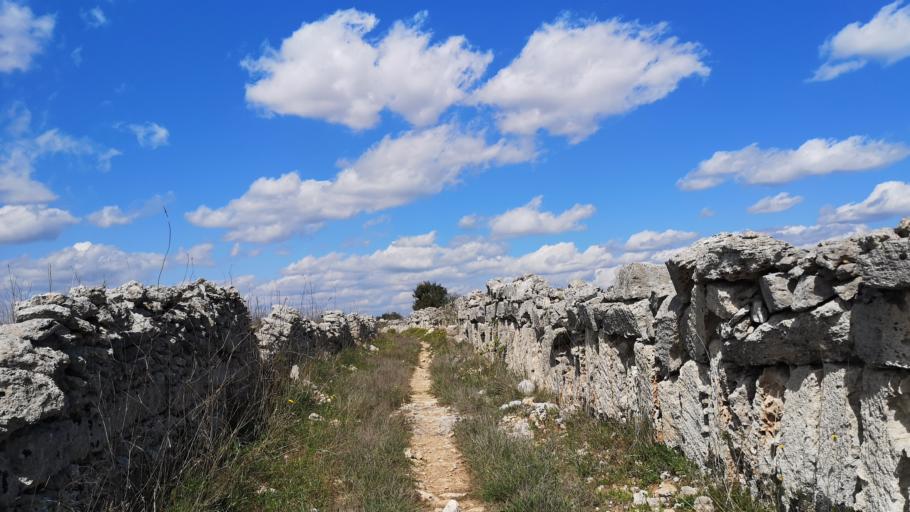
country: IT
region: Apulia
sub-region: Provincia di Lecce
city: Spongano
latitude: 40.0290
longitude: 18.3612
